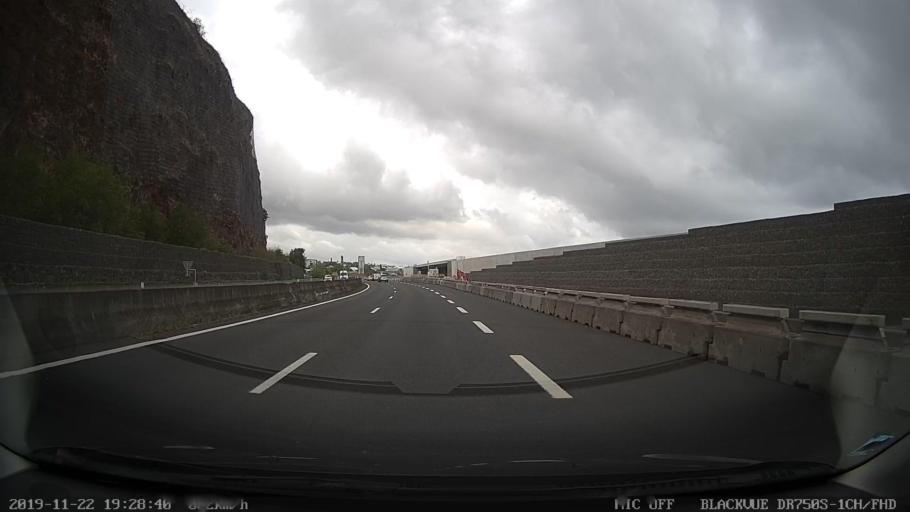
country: RE
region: Reunion
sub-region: Reunion
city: La Possession
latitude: -20.9196
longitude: 55.3475
